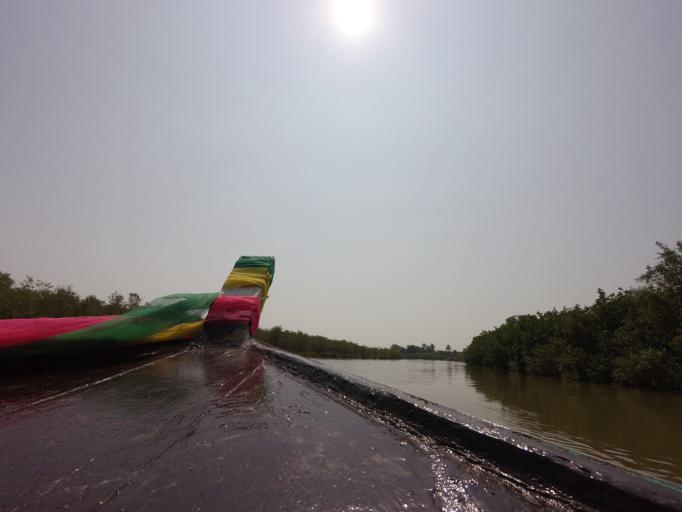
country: TH
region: Prachuap Khiri Khan
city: Kui Buri
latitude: 12.1362
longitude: 99.9673
